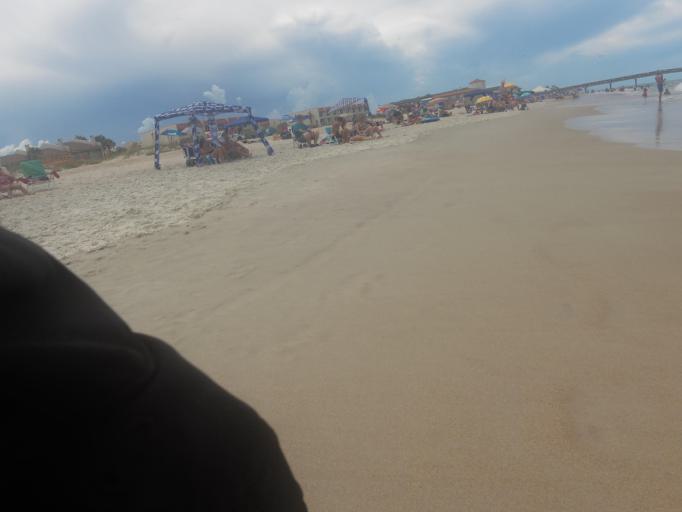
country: US
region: Florida
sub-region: Saint Johns County
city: Saint Augustine Beach
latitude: 29.8547
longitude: -81.2649
